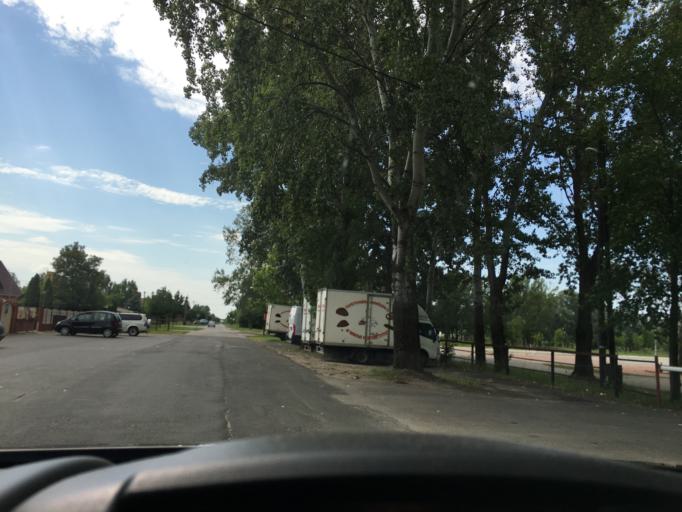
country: HU
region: Csongrad
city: Morahalom
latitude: 46.2172
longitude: 19.8705
